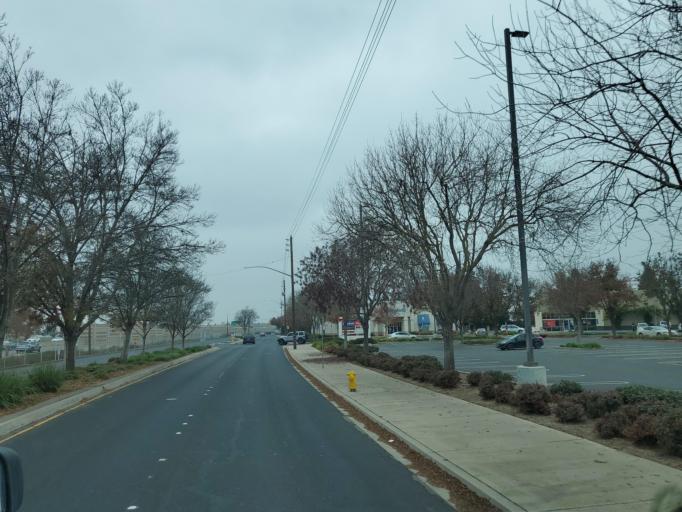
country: US
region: California
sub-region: Stanislaus County
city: Salida
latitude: 37.6949
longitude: -121.0665
